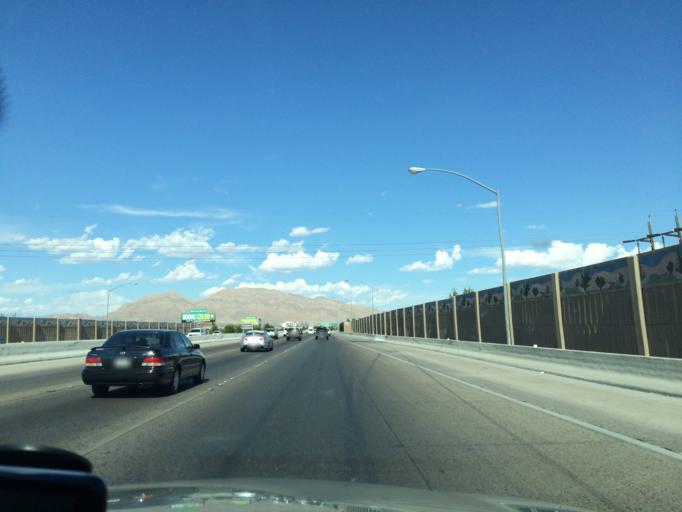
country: US
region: Nevada
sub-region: Clark County
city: Las Vegas
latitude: 36.1676
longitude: -115.1081
